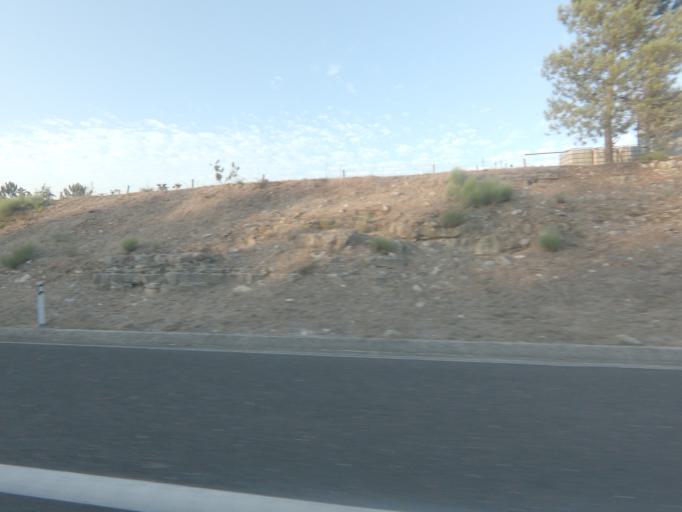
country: PT
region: Leiria
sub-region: Leiria
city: Santa Catarina da Serra
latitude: 39.7056
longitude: -8.7053
